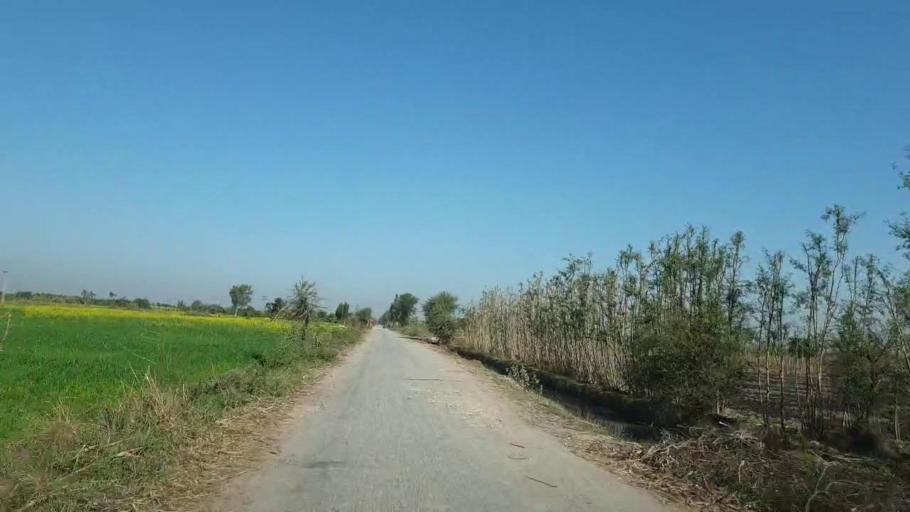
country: PK
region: Sindh
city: Mirpur Khas
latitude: 25.6060
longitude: 69.0244
